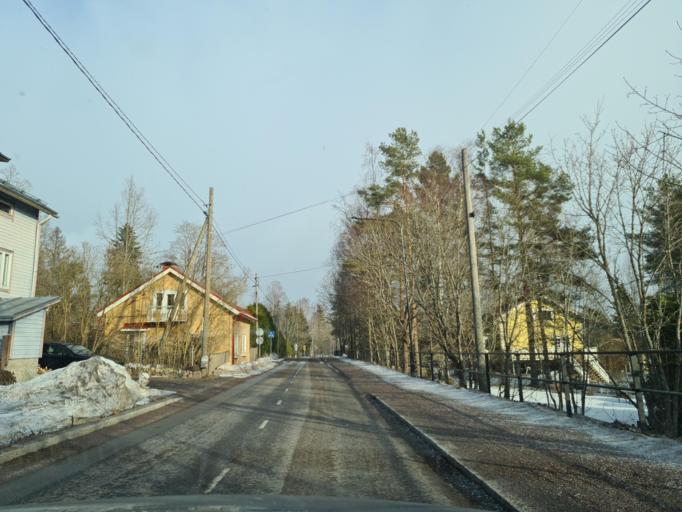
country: FI
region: Uusimaa
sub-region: Helsinki
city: Maentsaelae
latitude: 60.6396
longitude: 25.3118
